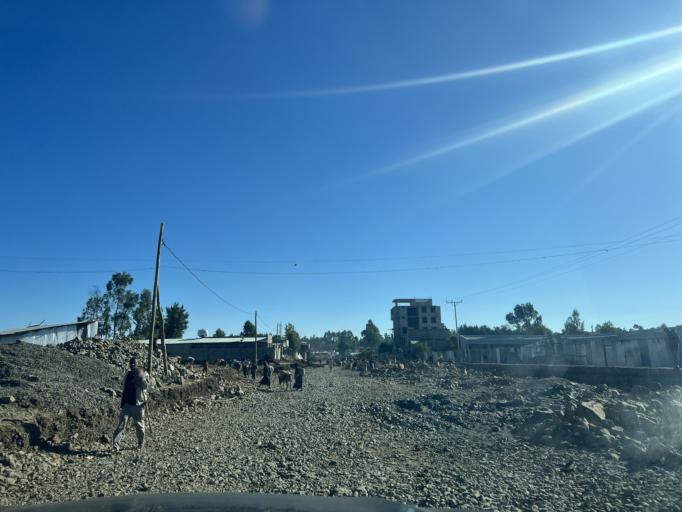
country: ET
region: Amhara
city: Were Ilu
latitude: 10.2010
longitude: 39.0816
